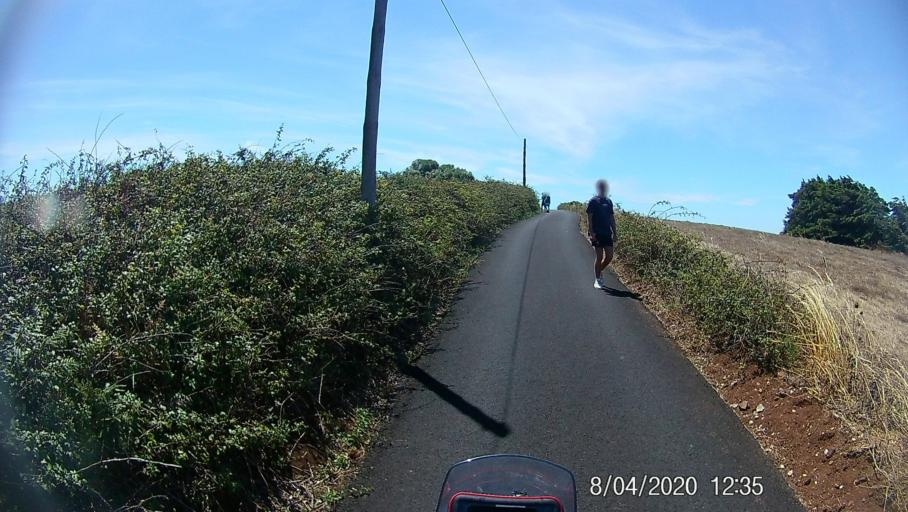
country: PT
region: Lisbon
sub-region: Sintra
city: Rio de Mouro
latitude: 38.7499
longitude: -9.3619
